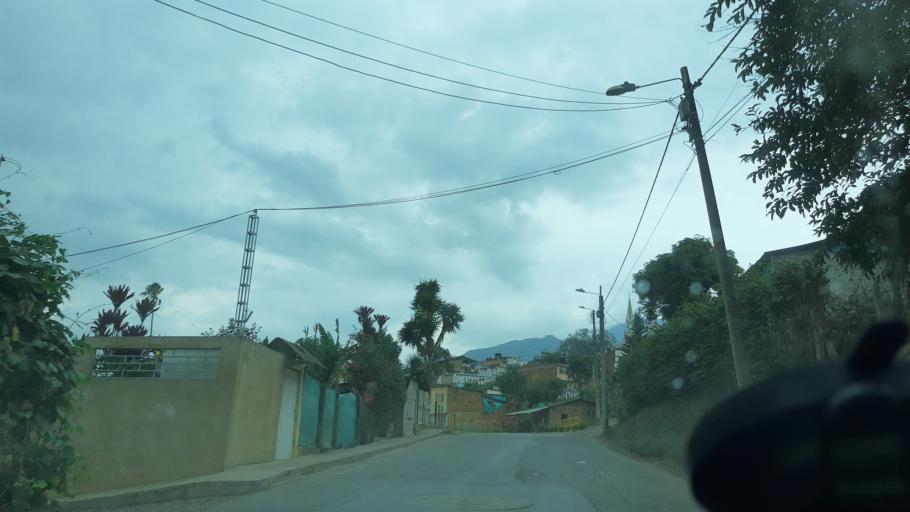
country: CO
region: Boyaca
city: Garagoa
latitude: 5.0799
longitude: -73.3666
